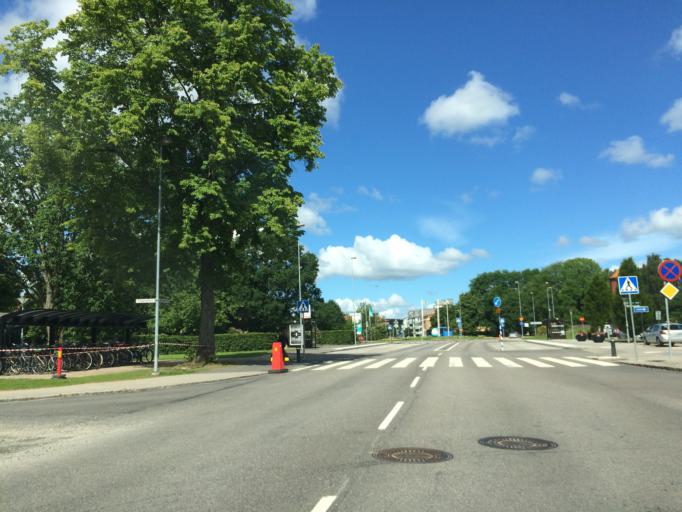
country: SE
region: Vaestra Goetaland
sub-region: Trollhattan
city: Trollhattan
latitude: 58.2868
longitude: 12.2987
